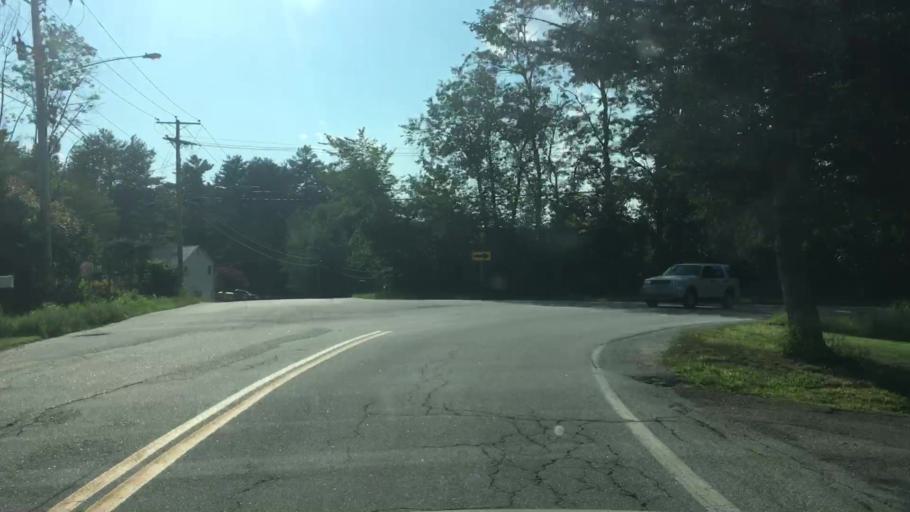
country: US
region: New Hampshire
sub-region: Belknap County
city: Gilford
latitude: 43.5646
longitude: -71.4283
